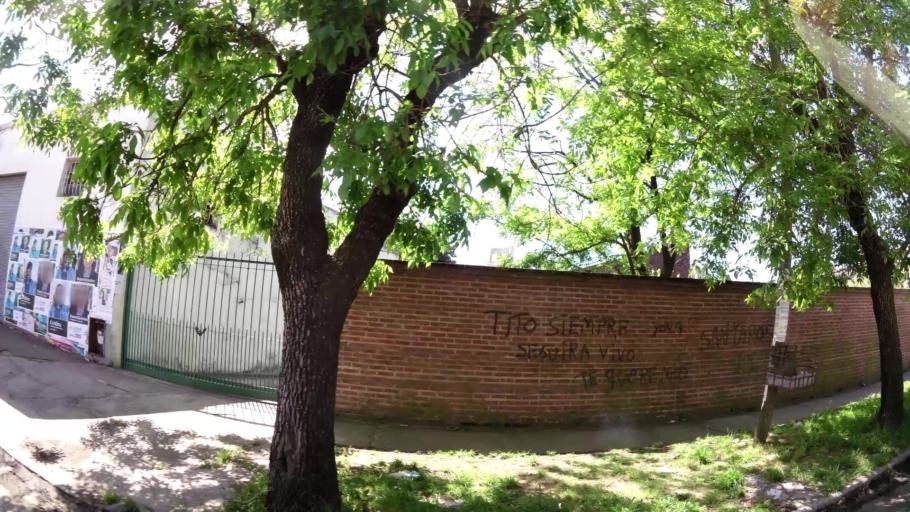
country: AR
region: Buenos Aires
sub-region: Partido de Quilmes
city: Quilmes
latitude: -34.8185
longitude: -58.2765
